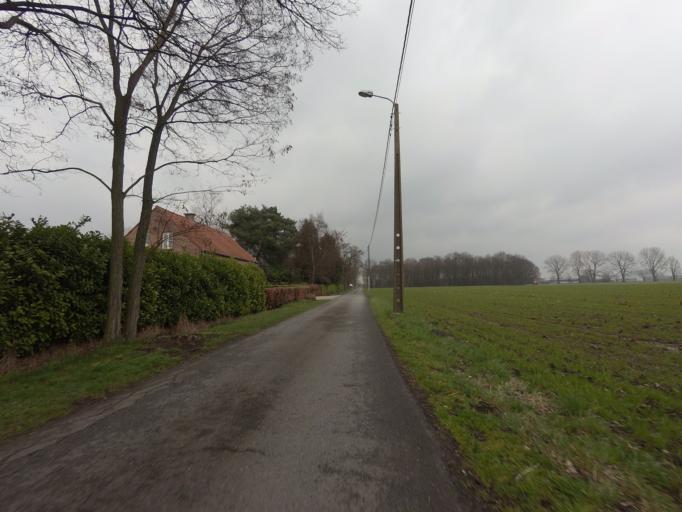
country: BE
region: Flanders
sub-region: Provincie Antwerpen
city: Putte
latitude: 51.0703
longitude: 4.5918
